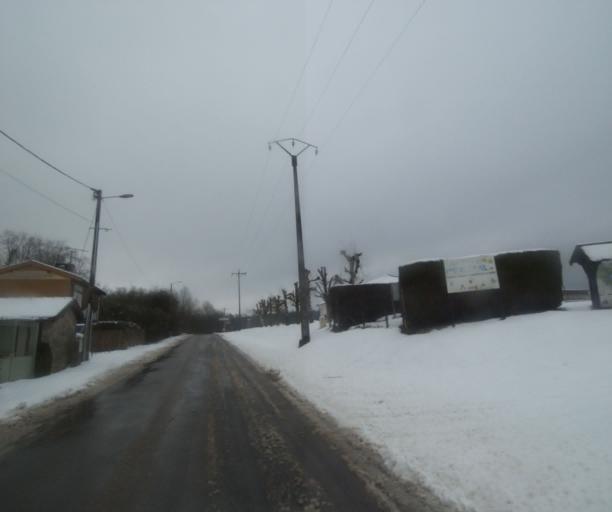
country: FR
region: Champagne-Ardenne
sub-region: Departement de la Haute-Marne
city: Laneuville-a-Remy
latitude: 48.4728
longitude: 4.8836
